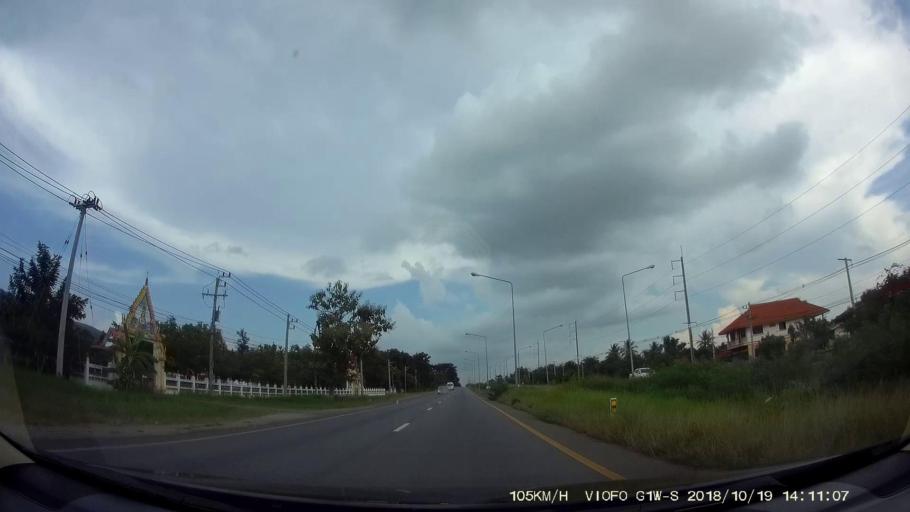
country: TH
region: Chaiyaphum
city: Khon Sawan
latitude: 15.9363
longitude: 102.1552
